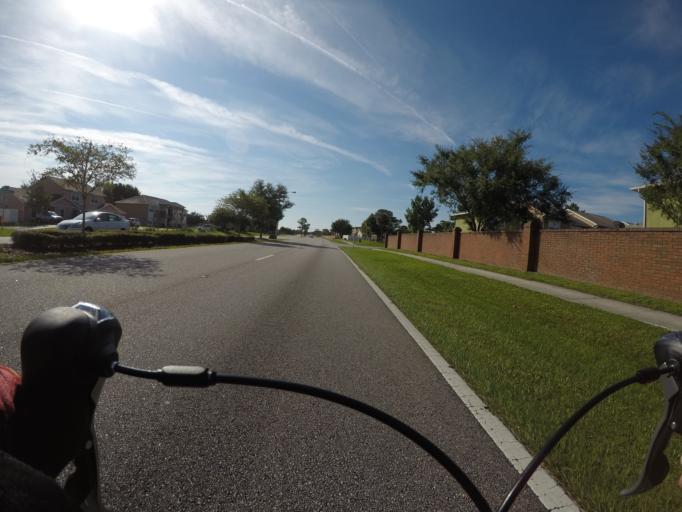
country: US
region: Florida
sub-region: Osceola County
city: Buenaventura Lakes
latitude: 28.3242
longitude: -81.3469
